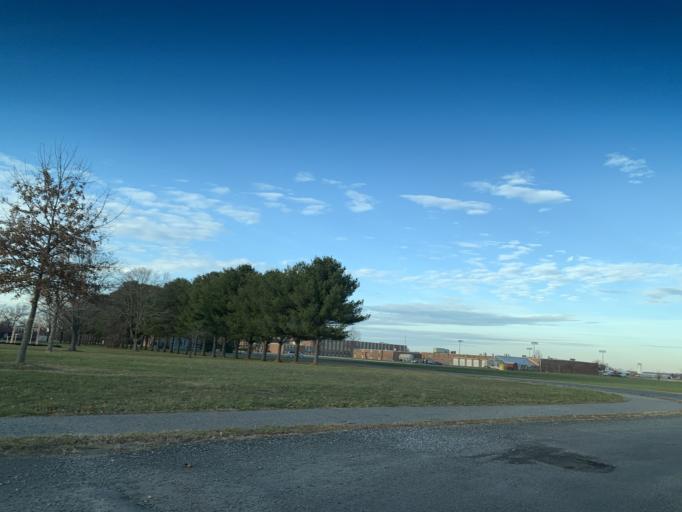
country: US
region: Maryland
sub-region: Kent County
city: Chestertown
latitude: 39.2824
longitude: -76.0917
